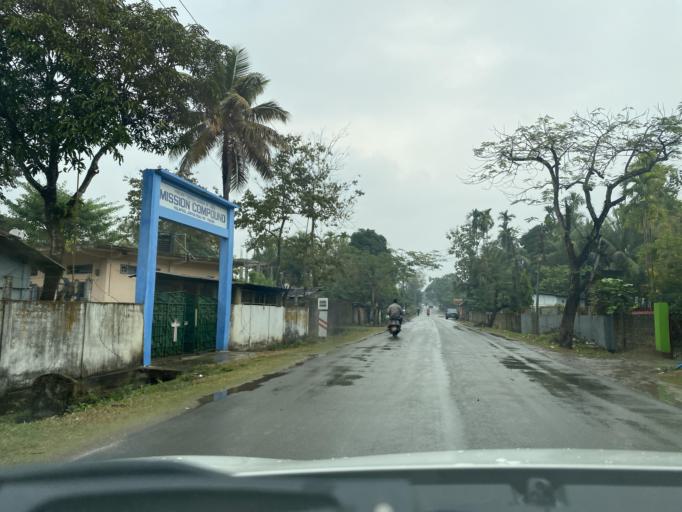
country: IN
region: Assam
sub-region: Cachar
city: Lakhipur
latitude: 24.8295
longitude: 93.0259
